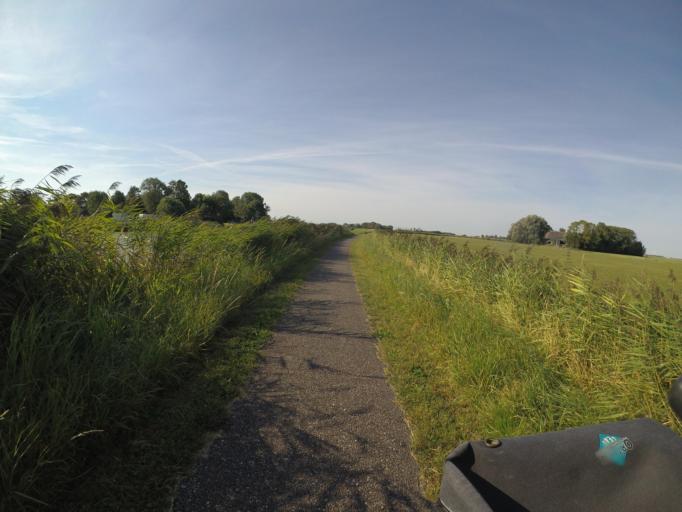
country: NL
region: Friesland
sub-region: Gemeente Dantumadiel
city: Rinsumageast
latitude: 53.3193
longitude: 5.9505
